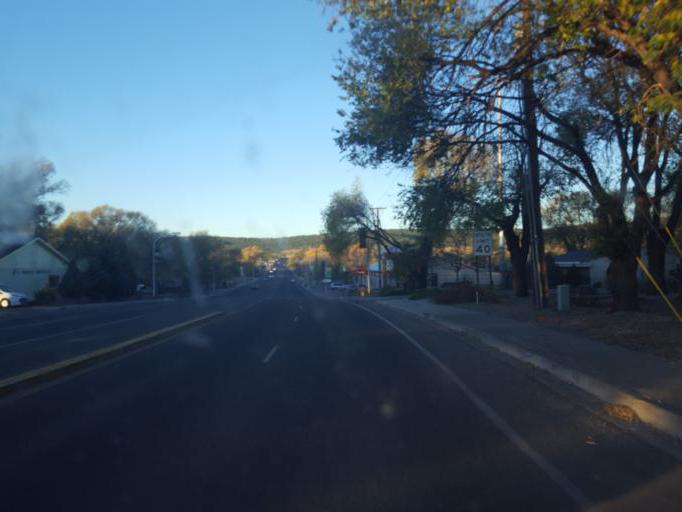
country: US
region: New Mexico
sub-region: San Miguel County
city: Las Vegas
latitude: 35.6049
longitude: -105.2246
